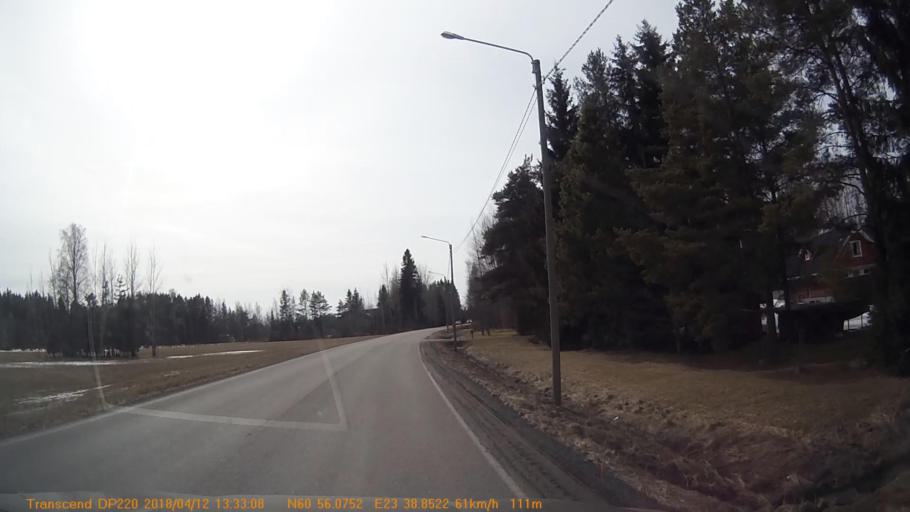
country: FI
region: Haeme
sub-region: Forssa
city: Forssa
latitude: 60.9345
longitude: 23.6474
